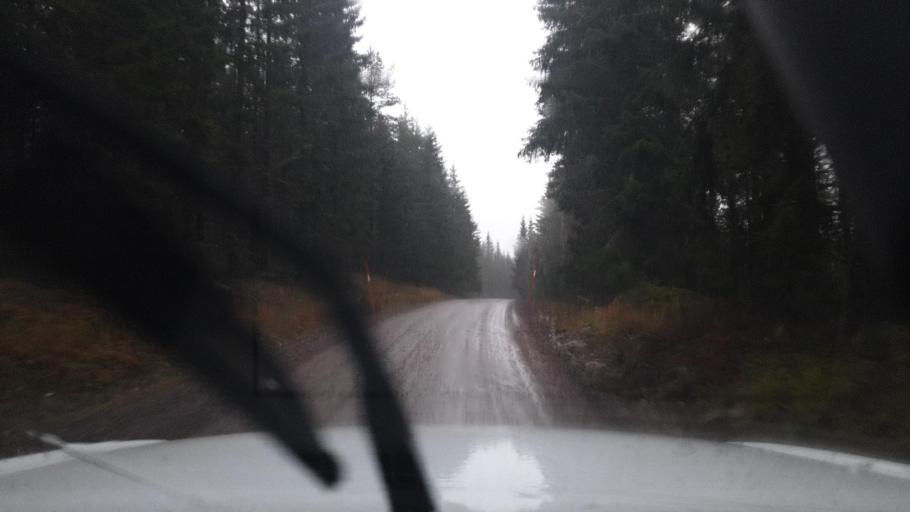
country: SE
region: Vaermland
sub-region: Arvika Kommun
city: Arvika
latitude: 59.9620
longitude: 12.6579
